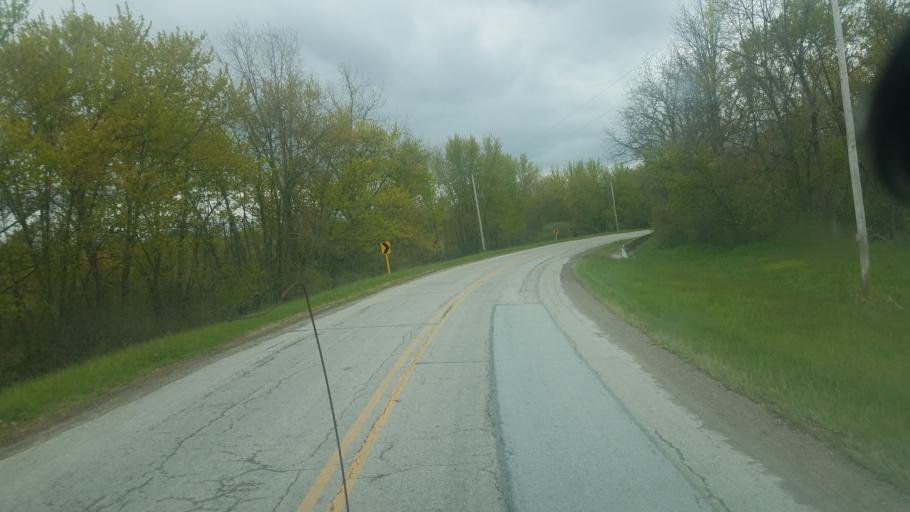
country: US
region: Ohio
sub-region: Marion County
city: Prospect
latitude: 40.5606
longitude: -83.2555
